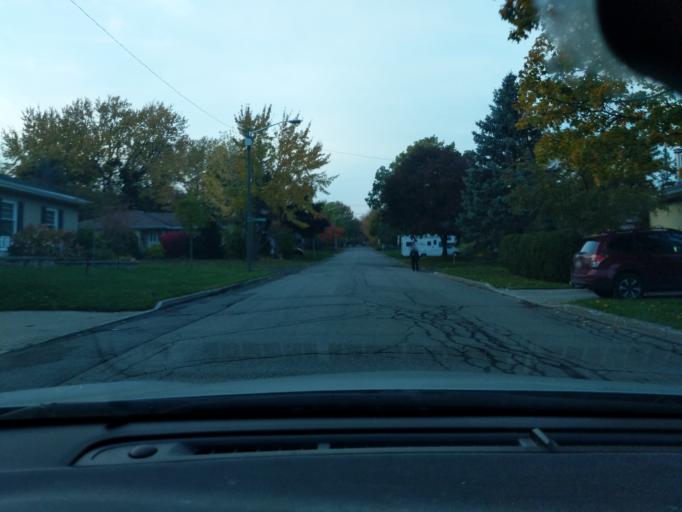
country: CA
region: Quebec
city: Quebec
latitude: 46.7623
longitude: -71.2766
